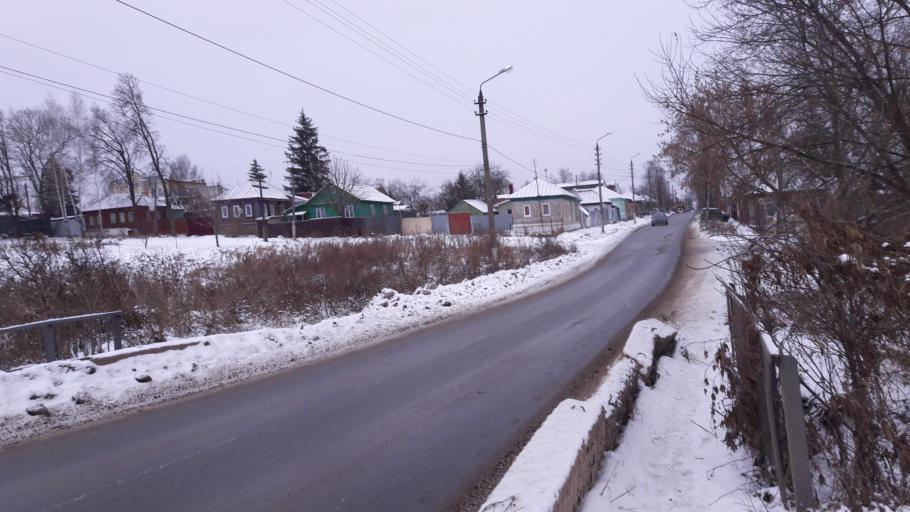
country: RU
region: Tula
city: Gorelki
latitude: 54.2375
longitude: 37.6321
